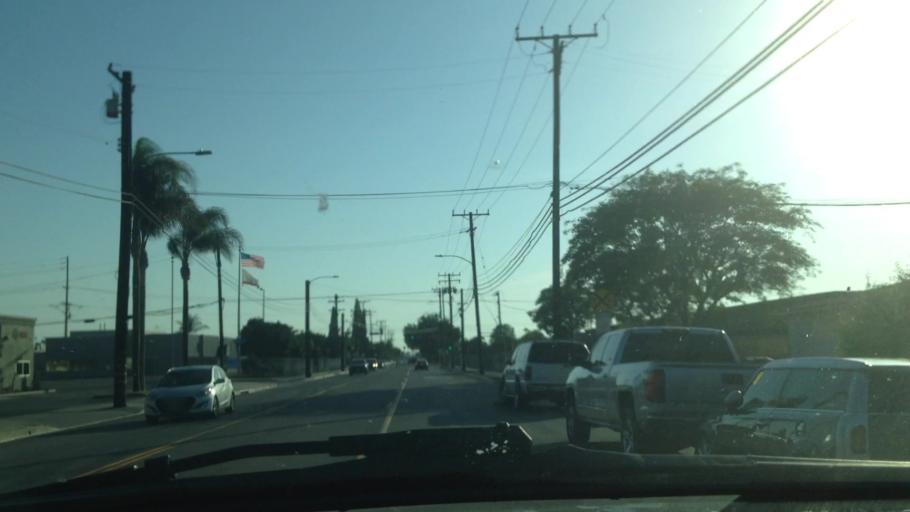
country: US
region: California
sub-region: Orange County
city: Anaheim
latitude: 33.8245
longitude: -117.9041
